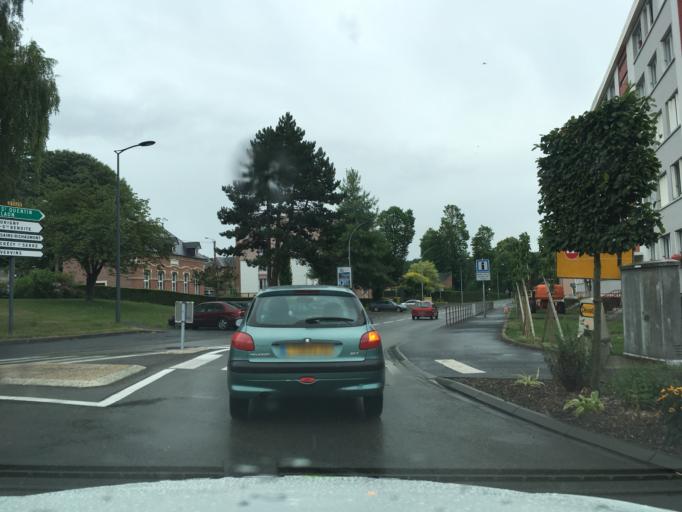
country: FR
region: Picardie
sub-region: Departement de l'Aisne
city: Guise
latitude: 49.9004
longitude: 3.6305
